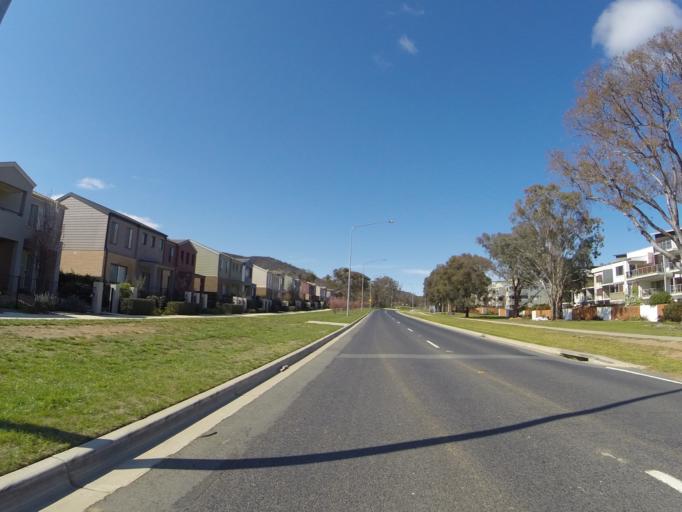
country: AU
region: Australian Capital Territory
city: Kaleen
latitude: -35.2266
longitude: 149.1660
